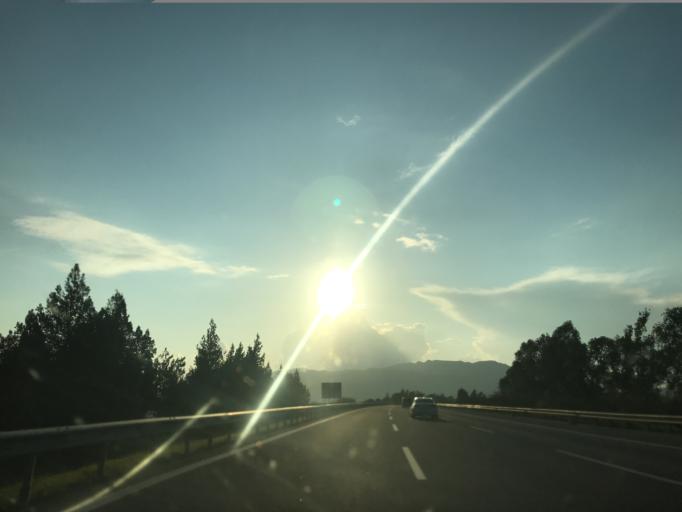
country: TR
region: Adana
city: Ceyhan
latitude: 36.9833
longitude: 35.7941
